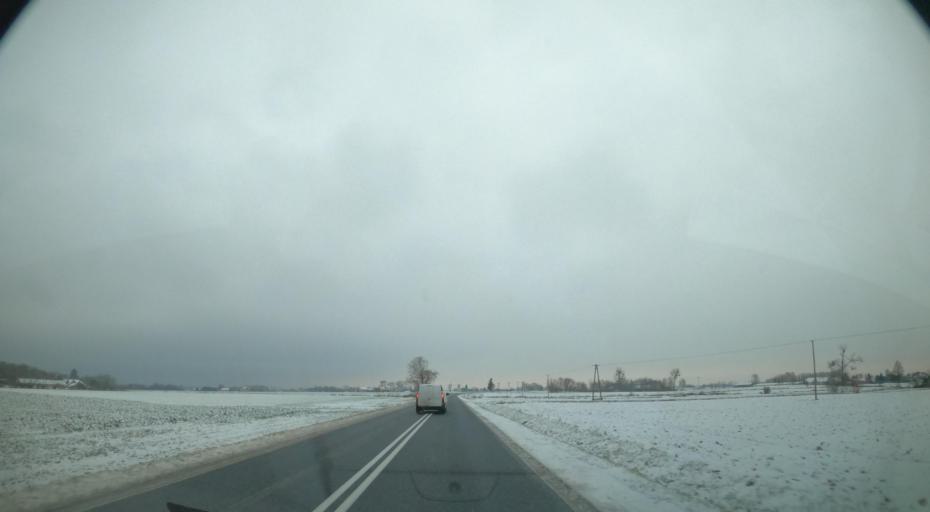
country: PL
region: Masovian Voivodeship
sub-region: Powiat plocki
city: Nowy Duninow
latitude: 52.6190
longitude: 19.4527
